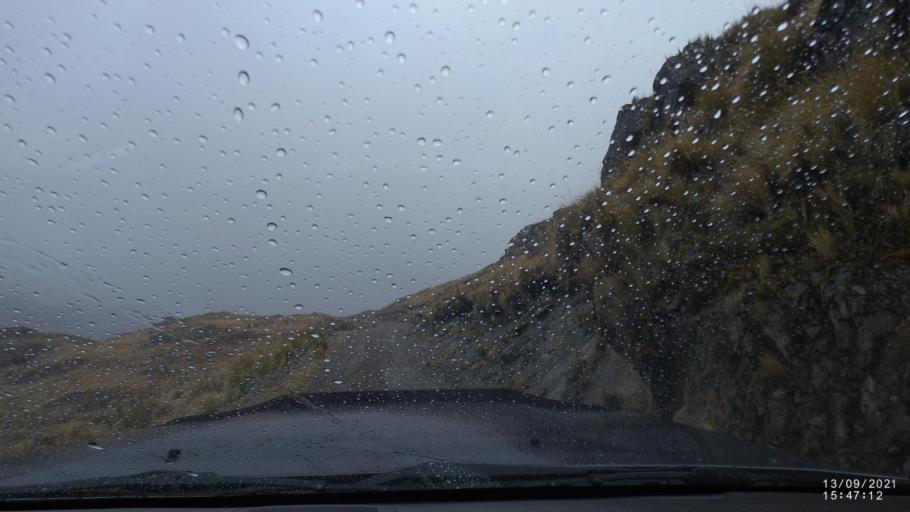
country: BO
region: Cochabamba
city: Colomi
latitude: -17.3138
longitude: -65.7189
